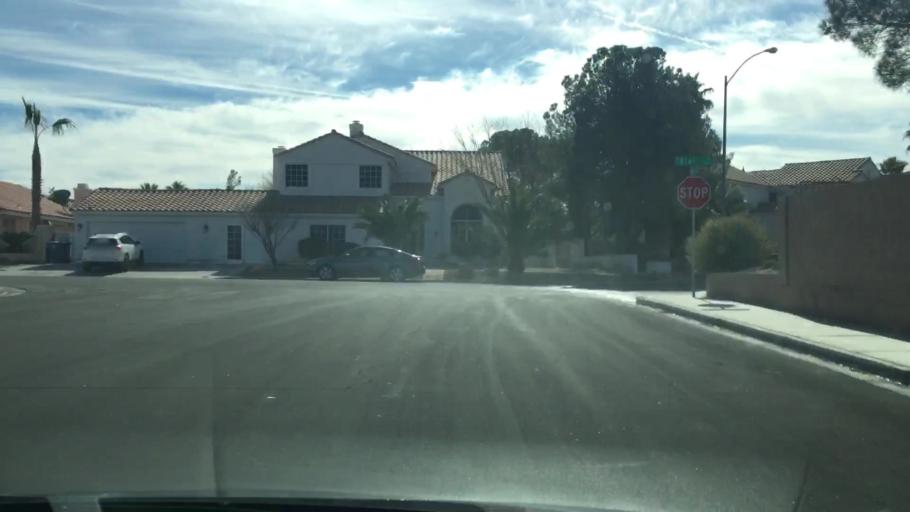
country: US
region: Nevada
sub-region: Clark County
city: Whitney
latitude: 36.0496
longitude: -115.1288
